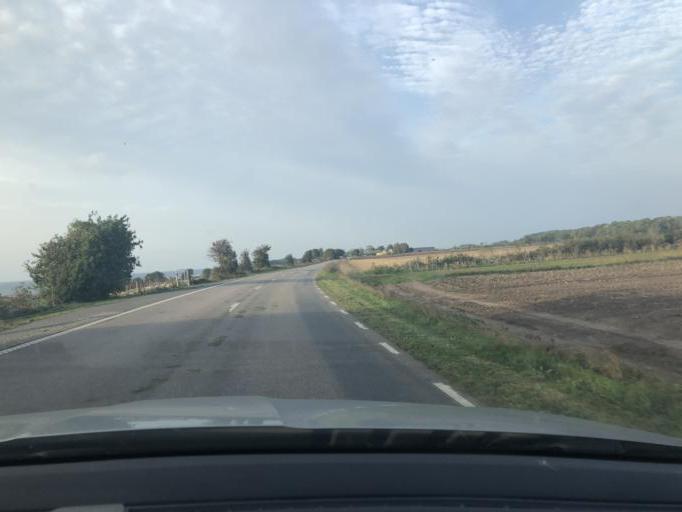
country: SE
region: Kalmar
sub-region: Morbylanga Kommun
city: Moerbylanga
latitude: 56.3152
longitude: 16.4057
